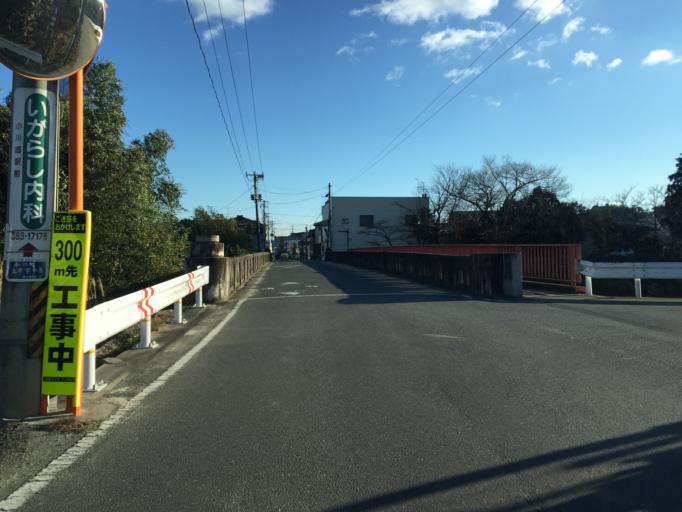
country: JP
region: Fukushima
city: Iwaki
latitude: 37.1289
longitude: 140.8608
